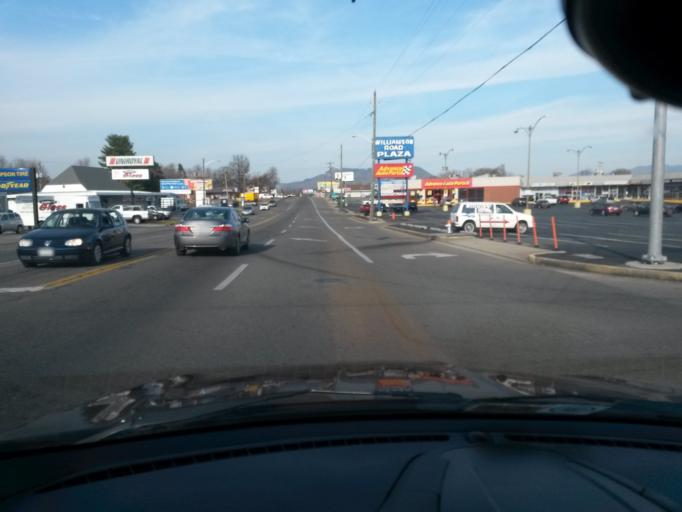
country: US
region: Virginia
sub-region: Roanoke County
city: Hollins
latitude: 37.3220
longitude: -79.9541
